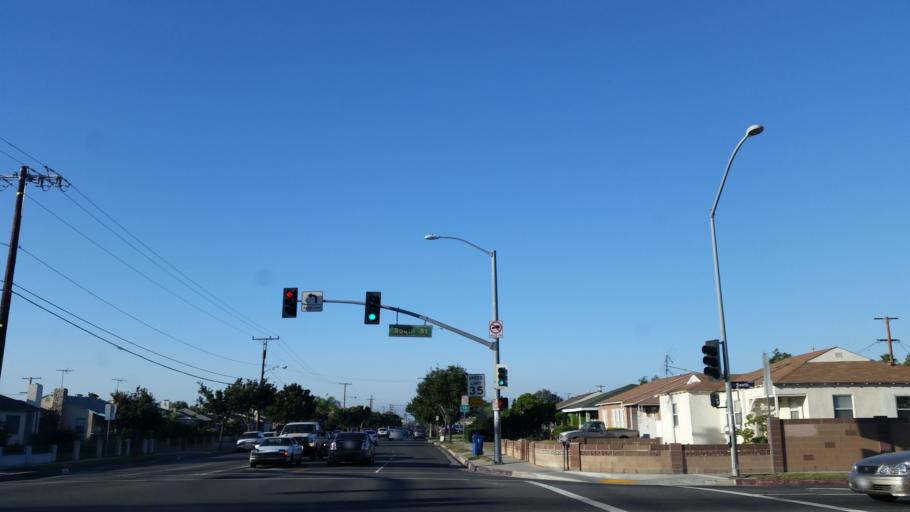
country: US
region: California
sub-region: Los Angeles County
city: Lakewood
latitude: 33.8602
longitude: -118.1337
